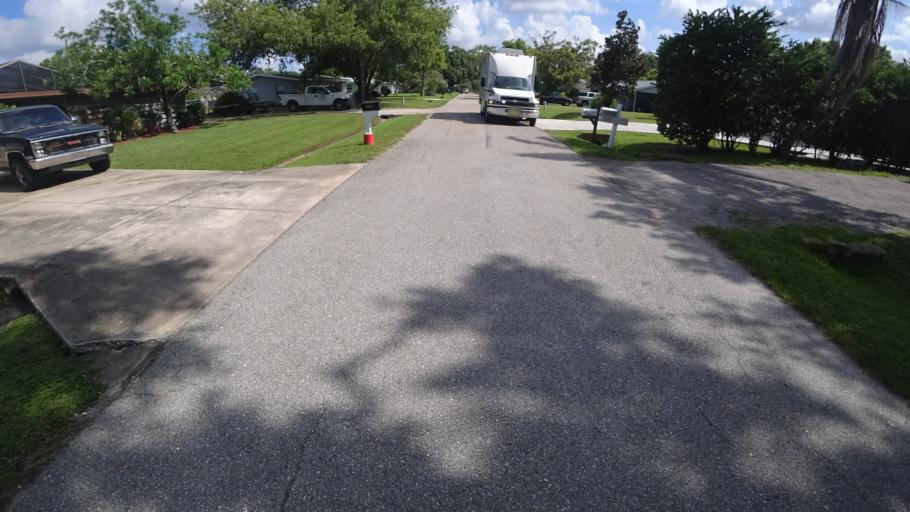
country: US
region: Florida
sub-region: Manatee County
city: Samoset
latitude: 27.4409
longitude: -82.5352
